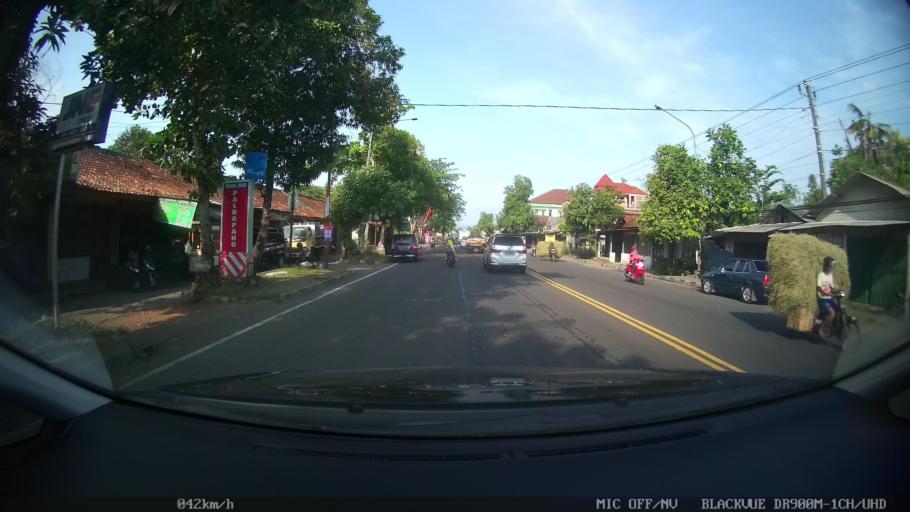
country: ID
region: Daerah Istimewa Yogyakarta
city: Bantul
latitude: -7.9055
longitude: 110.3189
